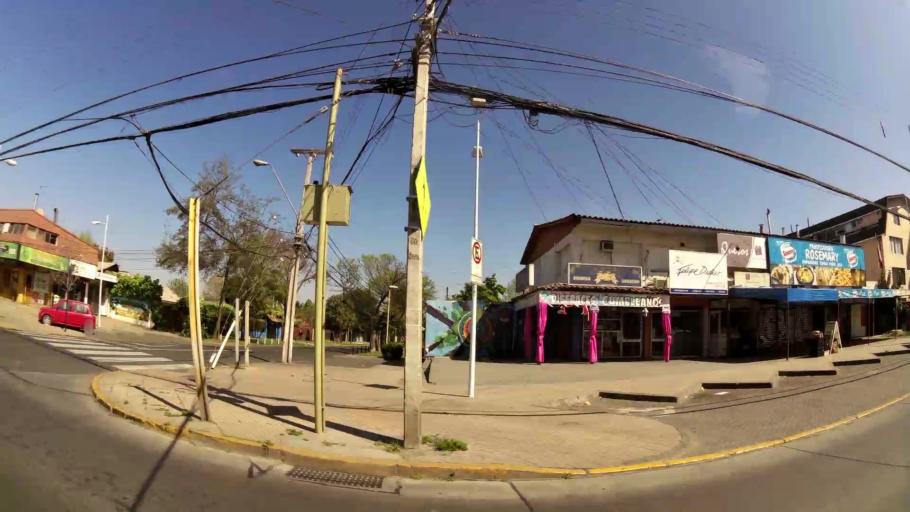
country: CL
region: Santiago Metropolitan
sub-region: Provincia de Santiago
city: Villa Presidente Frei, Nunoa, Santiago, Chile
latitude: -33.4293
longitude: -70.5543
